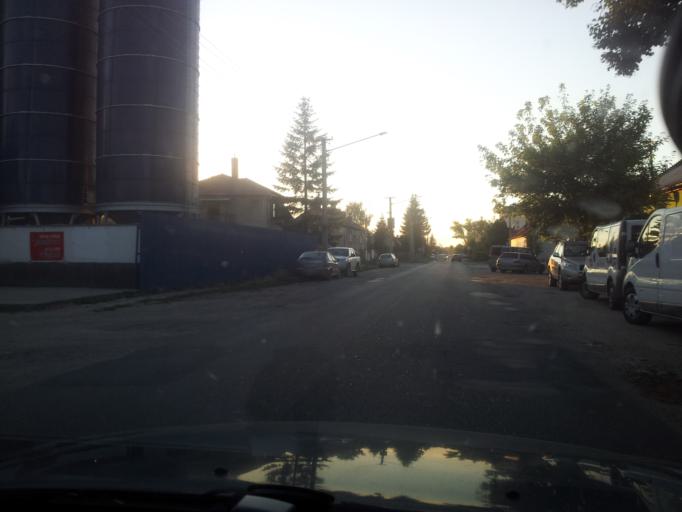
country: SK
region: Nitriansky
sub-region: Okres Nove Zamky
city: Sturovo
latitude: 47.8013
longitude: 18.7128
